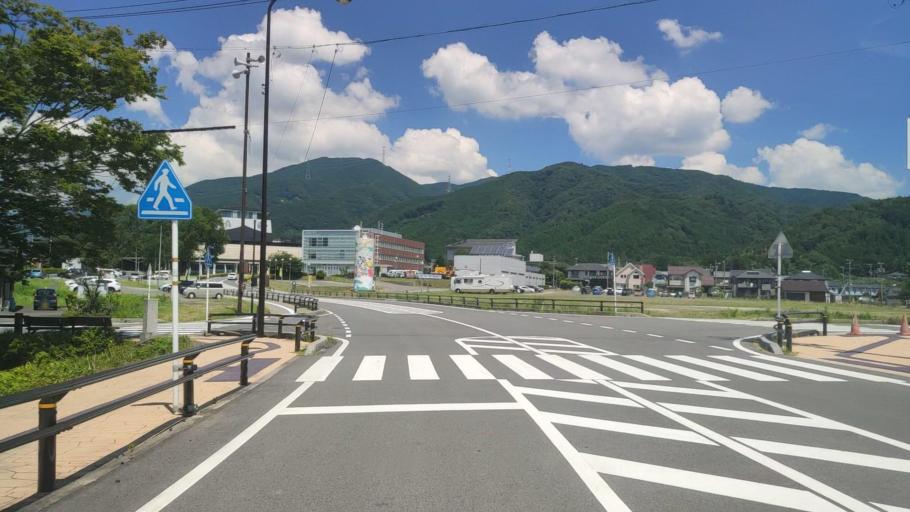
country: JP
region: Gifu
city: Tarui
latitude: 35.3639
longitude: 136.4684
